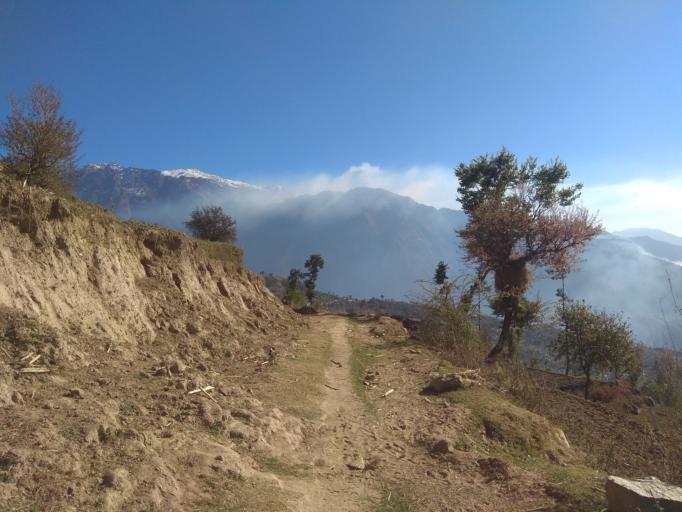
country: NP
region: Far Western
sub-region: Seti Zone
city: Achham
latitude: 29.2570
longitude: 81.6342
